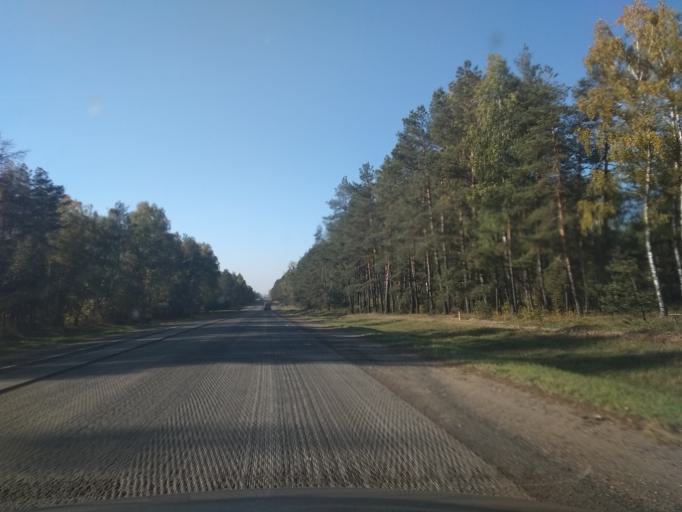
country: BY
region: Grodnenskaya
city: Zhyrovichy
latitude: 53.0598
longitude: 25.4320
